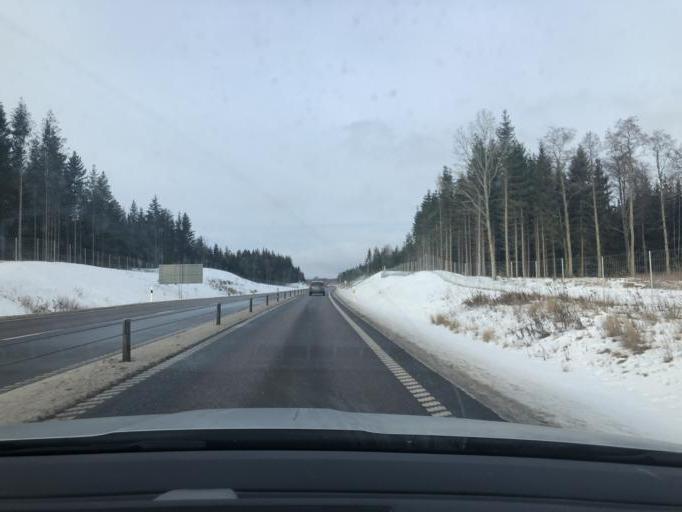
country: SE
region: OEstergoetland
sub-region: Motala Kommun
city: Borensberg
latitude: 58.5857
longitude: 15.1983
